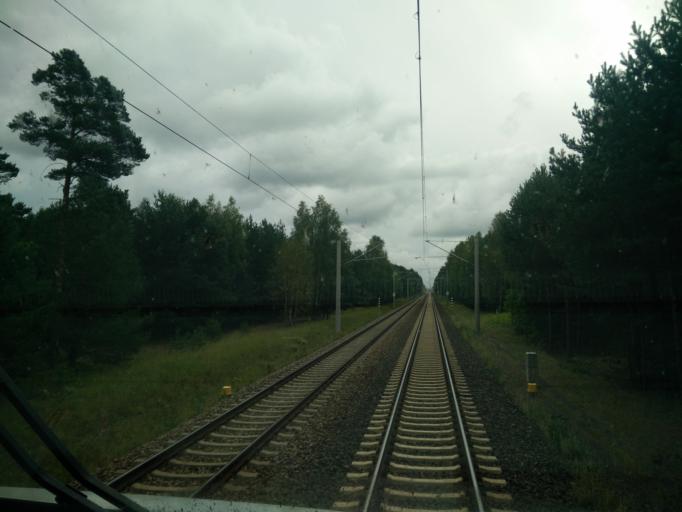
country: DE
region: Brandenburg
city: Gross Koris
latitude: 52.1430
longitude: 13.6652
